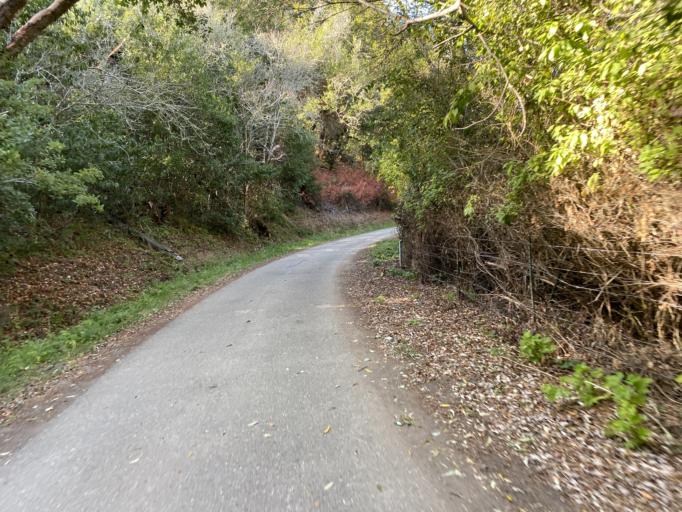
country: US
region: California
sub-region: San Mateo County
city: Hillsborough
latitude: 37.5679
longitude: -122.4025
